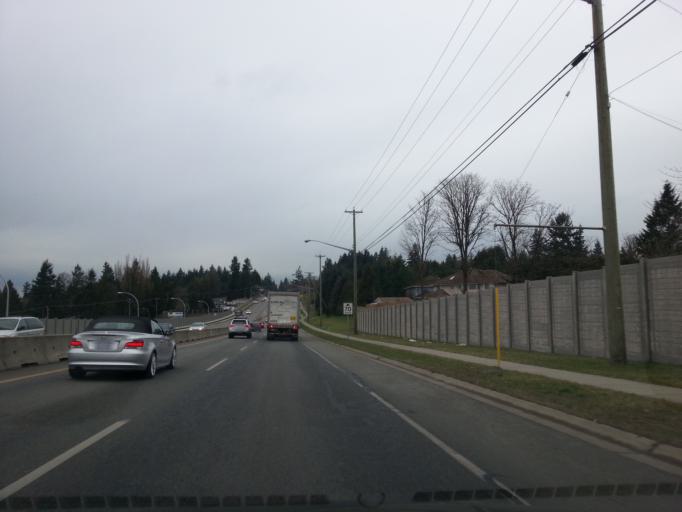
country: CA
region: British Columbia
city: Surrey
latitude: 49.1045
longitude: -122.8183
